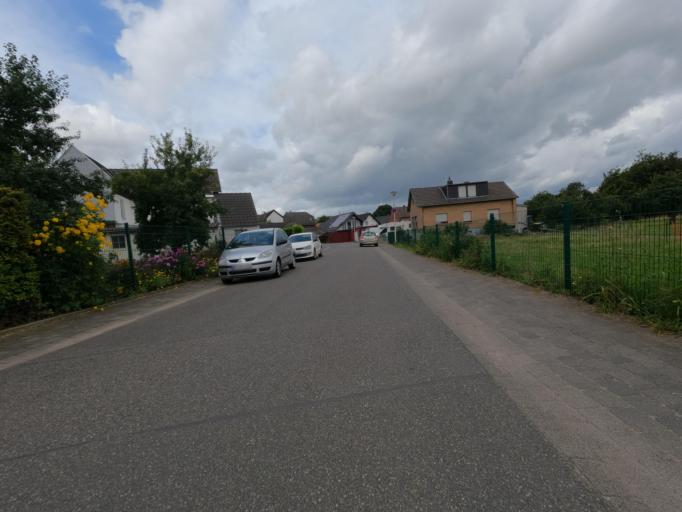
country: DE
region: North Rhine-Westphalia
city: Huckelhoven
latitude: 51.0165
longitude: 6.1785
